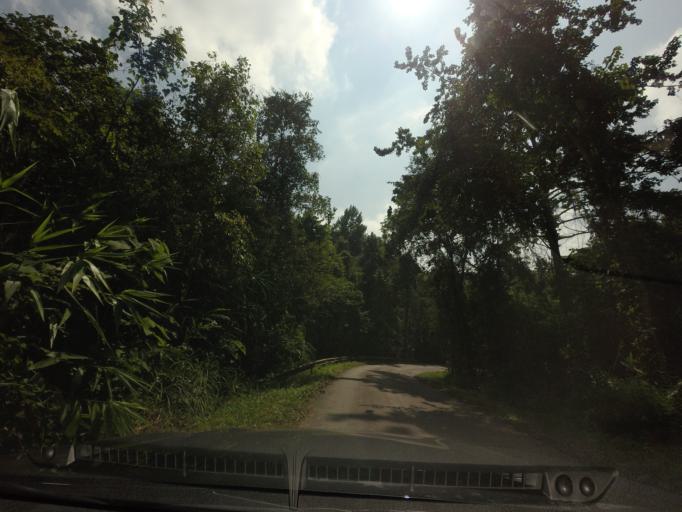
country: TH
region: Loei
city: Na Haeo
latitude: 17.4815
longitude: 100.9395
